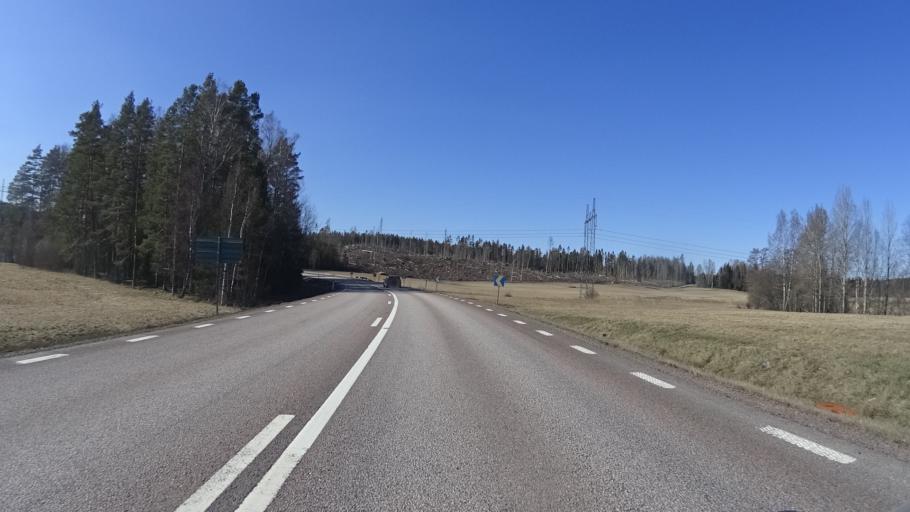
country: SE
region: Vaermland
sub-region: Karlstads Kommun
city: Edsvalla
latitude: 59.5224
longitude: 13.1575
